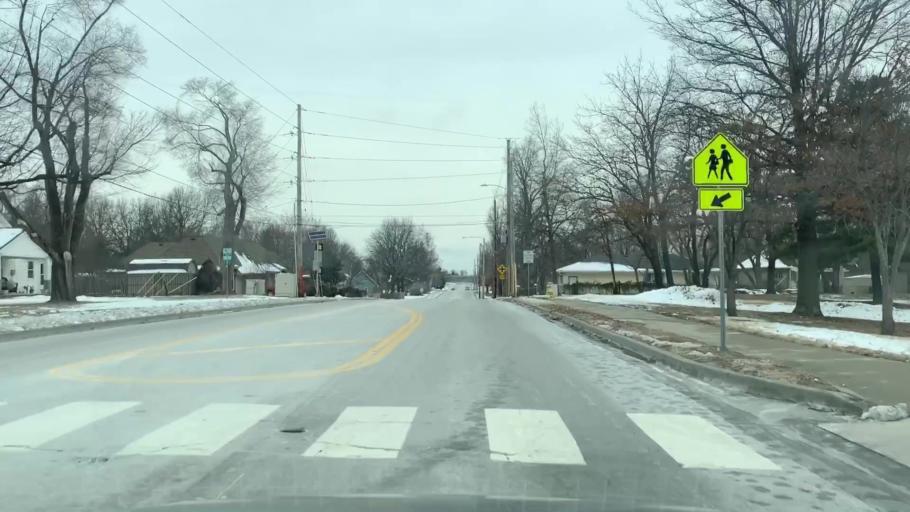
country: US
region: Missouri
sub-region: Jackson County
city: Lees Summit
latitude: 38.9385
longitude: -94.3644
